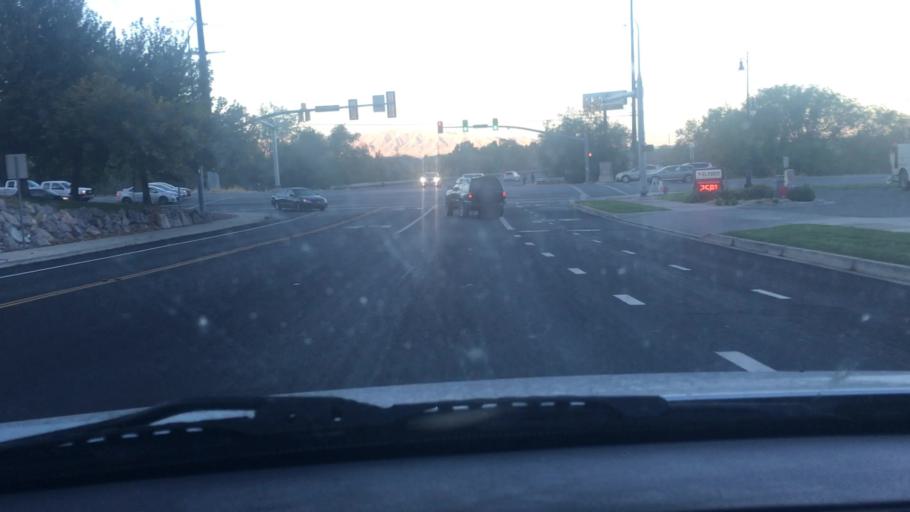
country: US
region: Utah
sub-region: Utah County
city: Provo
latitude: 40.2080
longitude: -111.6290
